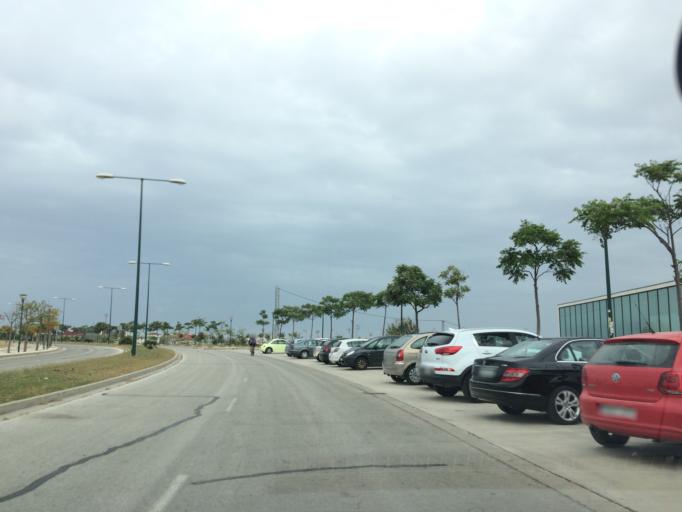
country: ES
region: Andalusia
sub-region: Provincia de Malaga
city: Malaga
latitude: 36.7152
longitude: -4.4996
